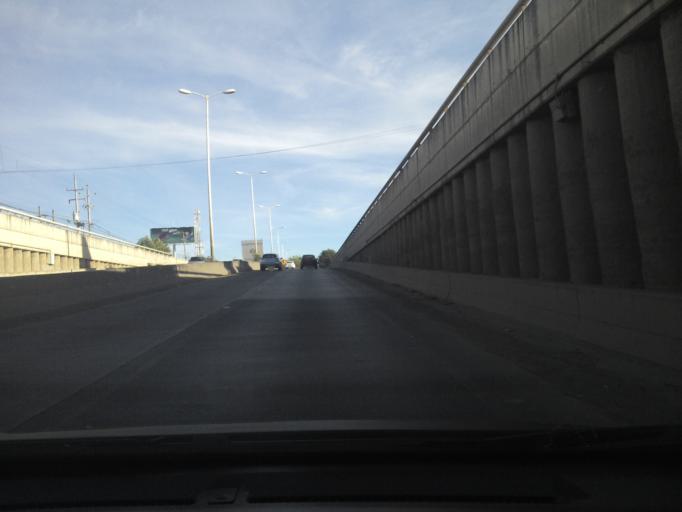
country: MX
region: Jalisco
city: Nuevo Mexico
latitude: 20.7089
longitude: -103.4664
